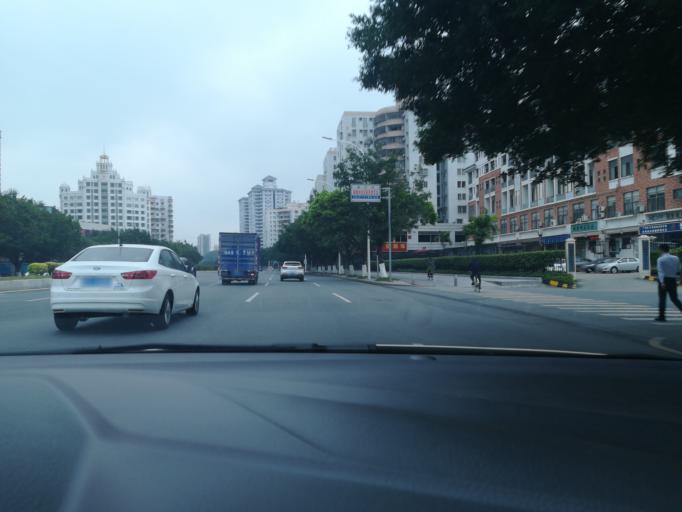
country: CN
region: Guangdong
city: Nansha
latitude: 22.8011
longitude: 113.5530
